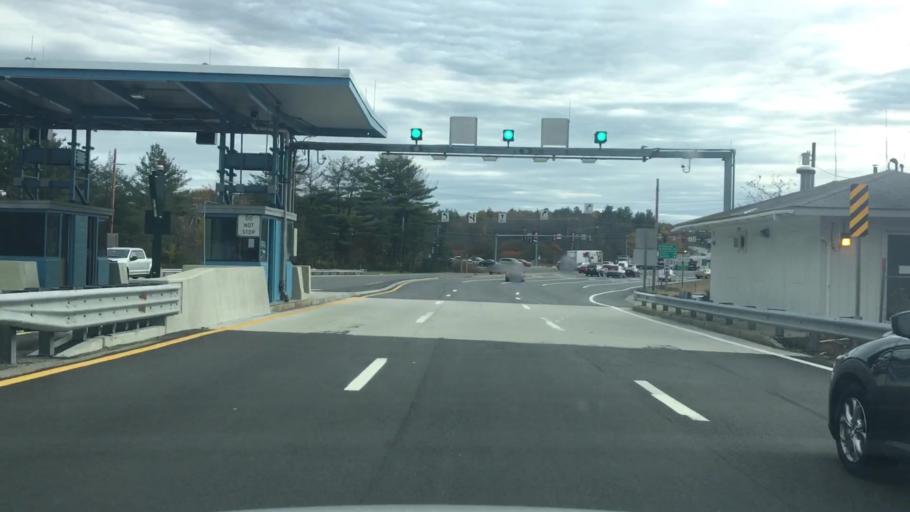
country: US
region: Maine
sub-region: York County
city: Biddeford
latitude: 43.4791
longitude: -70.4976
